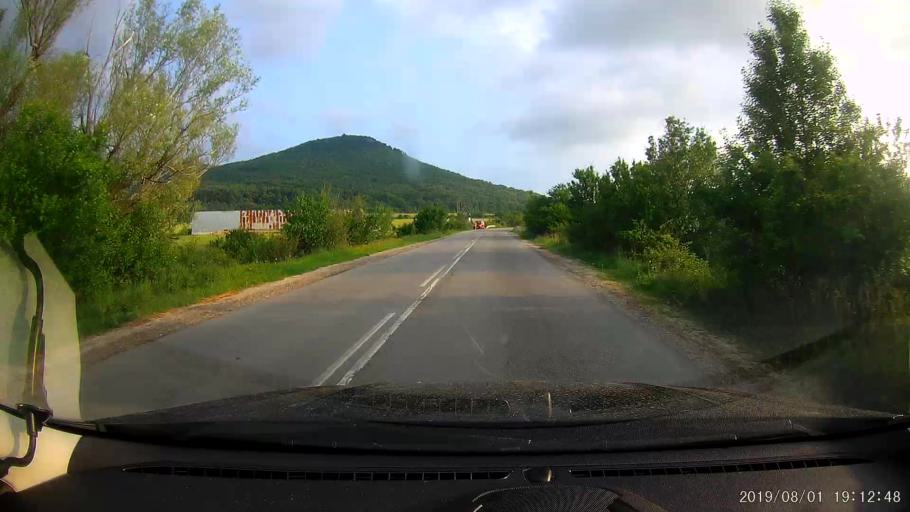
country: BG
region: Shumen
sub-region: Obshtina Smyadovo
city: Smyadovo
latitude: 42.9595
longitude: 26.9477
